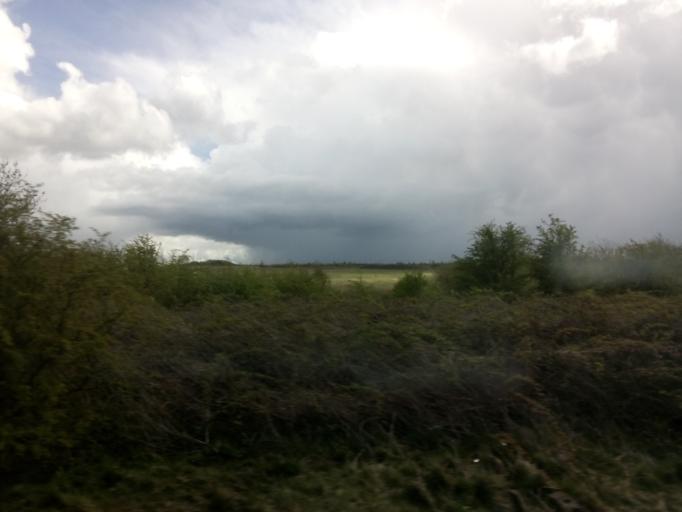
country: GB
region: Scotland
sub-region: East Lothian
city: Tranent
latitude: 55.9585
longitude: -2.9497
